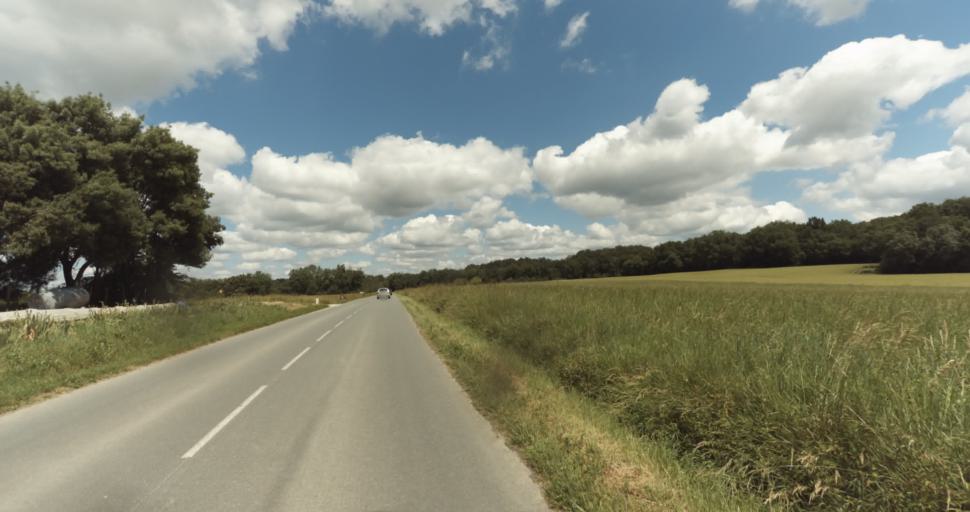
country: FR
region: Aquitaine
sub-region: Departement de la Dordogne
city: Beaumont-du-Perigord
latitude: 44.7075
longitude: 0.7499
